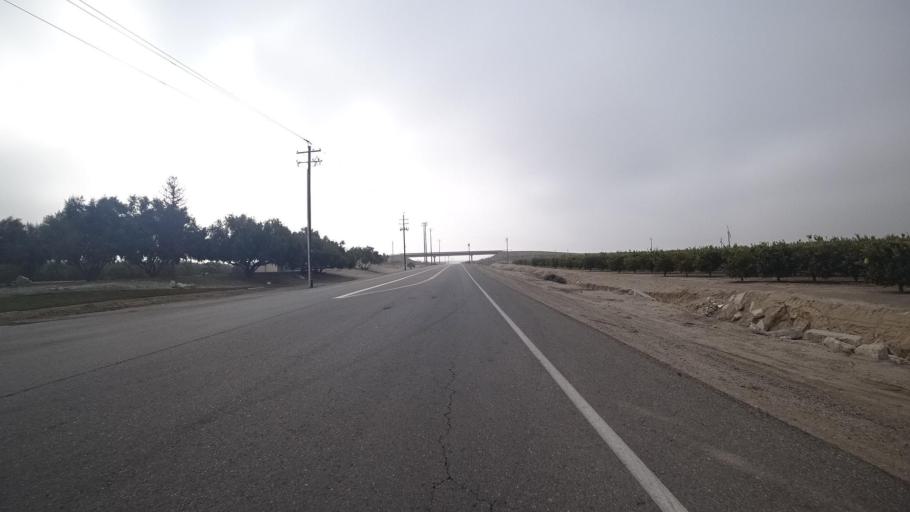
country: US
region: California
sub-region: Kern County
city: Pine Mountain Club
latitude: 35.0692
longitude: -119.1315
